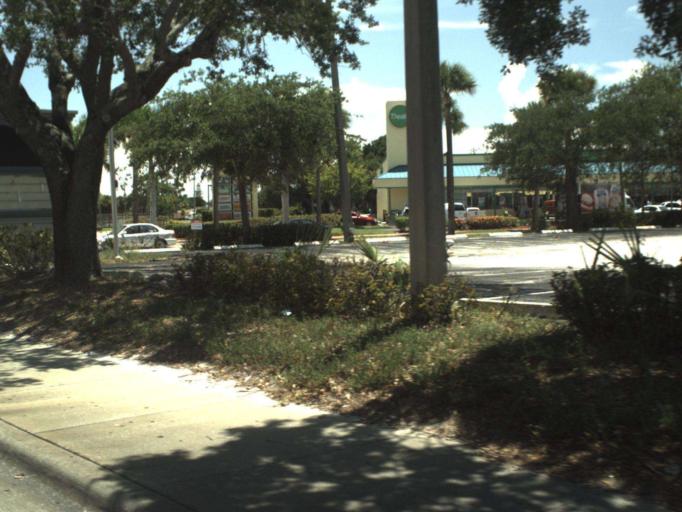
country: US
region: Florida
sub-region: Saint Lucie County
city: Fort Pierce
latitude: 27.4400
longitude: -80.3260
